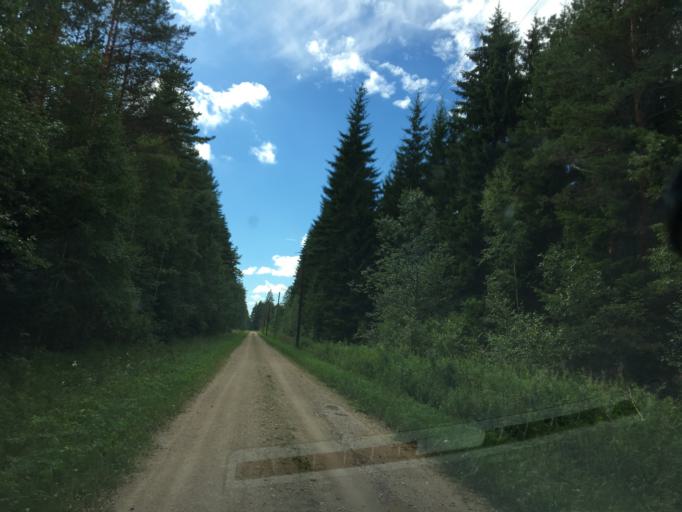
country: EE
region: Viljandimaa
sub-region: Suure-Jaani vald
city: Suure-Jaani
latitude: 58.5868
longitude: 25.2563
